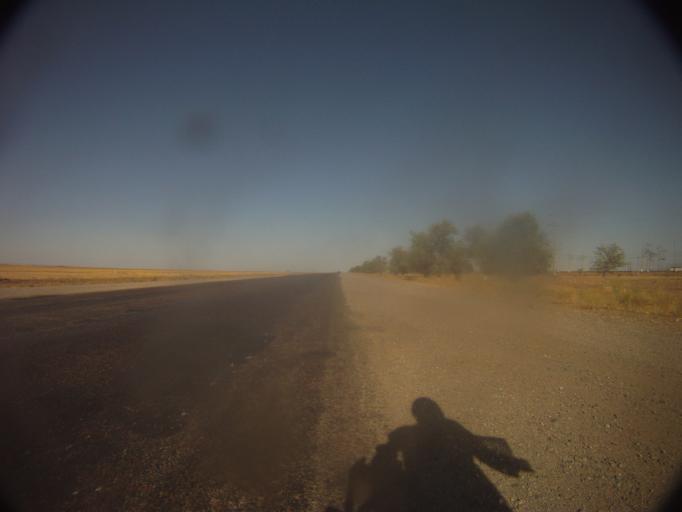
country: KZ
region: Zhambyl
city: Sarykemer
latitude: 42.9629
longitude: 71.5486
